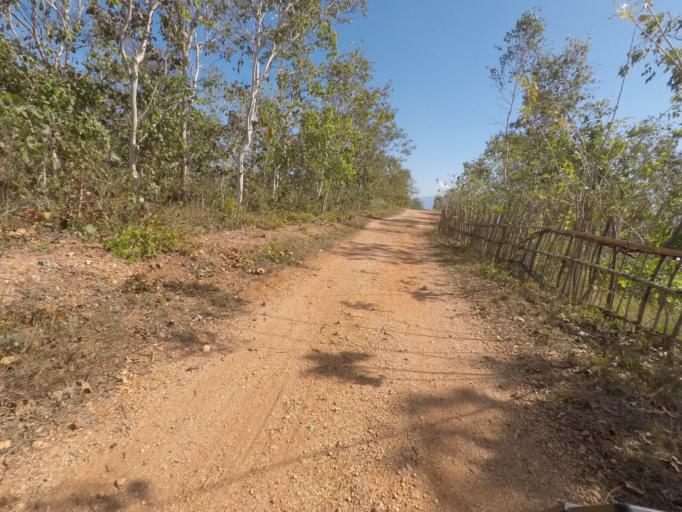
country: TL
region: Bobonaro
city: Maliana
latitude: -8.9515
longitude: 125.2156
